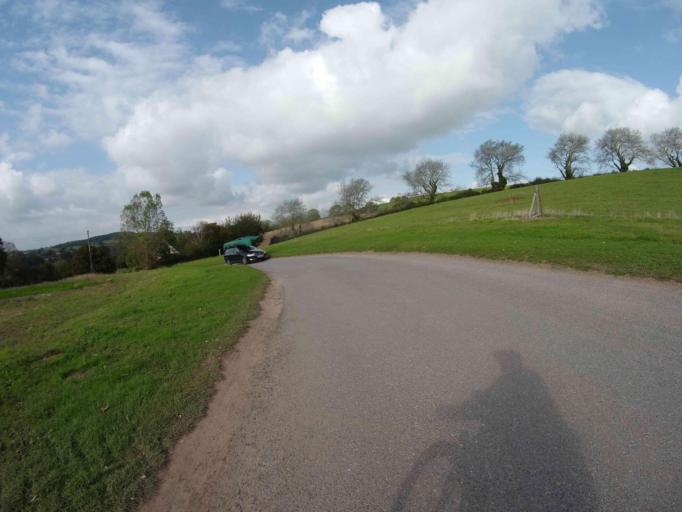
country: GB
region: England
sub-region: Devon
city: Budleigh Salterton
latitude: 50.6390
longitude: -3.3058
